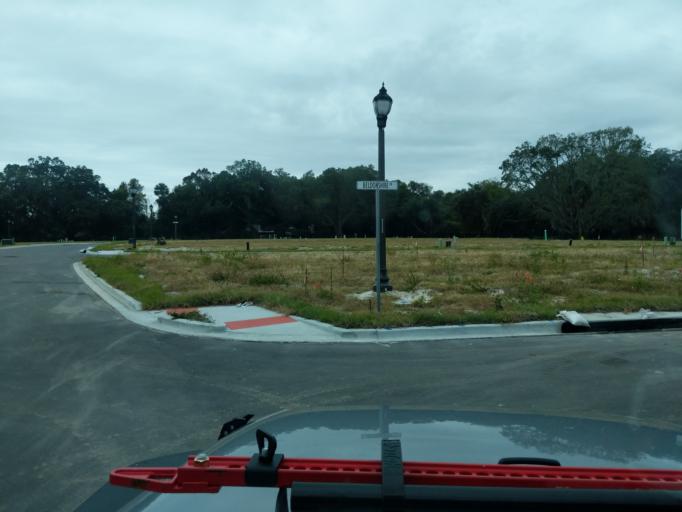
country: US
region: Florida
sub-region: Orange County
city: Oakland
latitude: 28.5542
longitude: -81.6158
